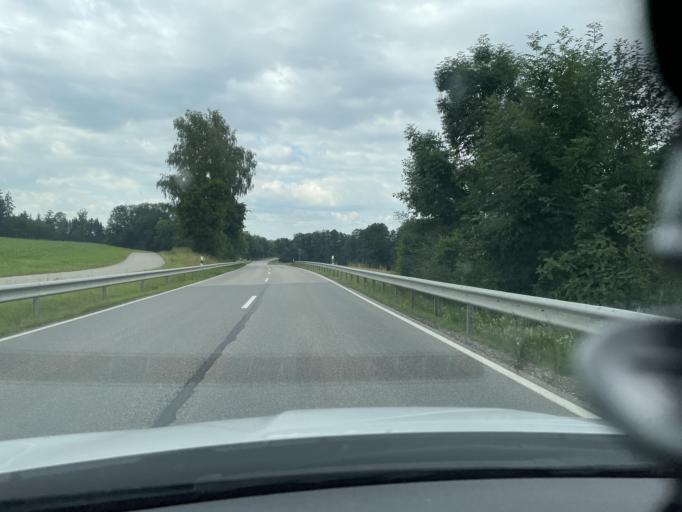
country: DE
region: Bavaria
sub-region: Upper Bavaria
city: Sankt Wolfgang
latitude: 48.1903
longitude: 12.1472
